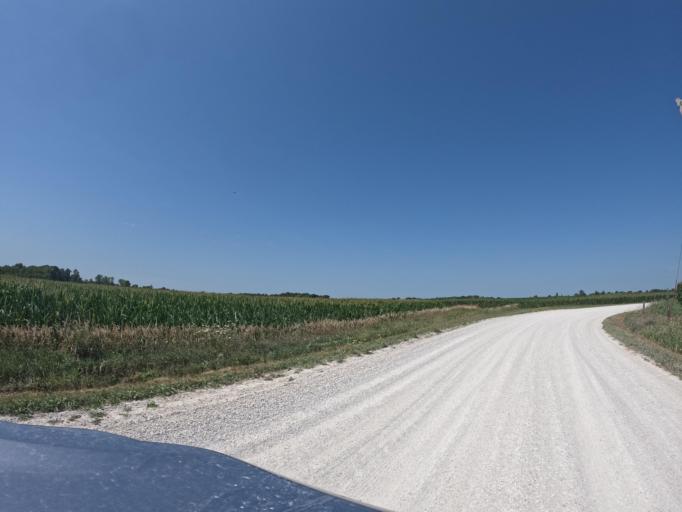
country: US
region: Iowa
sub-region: Henry County
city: Mount Pleasant
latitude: 40.8872
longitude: -91.5736
